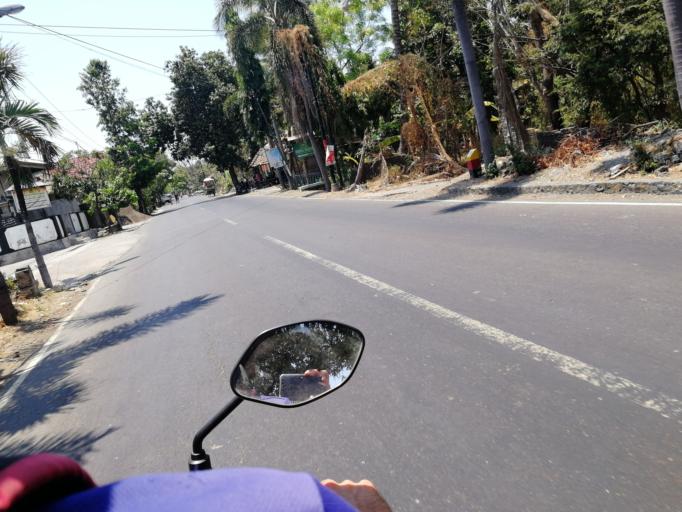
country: ID
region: Bali
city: Banjar Trunyan
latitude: -8.1516
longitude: 115.4129
